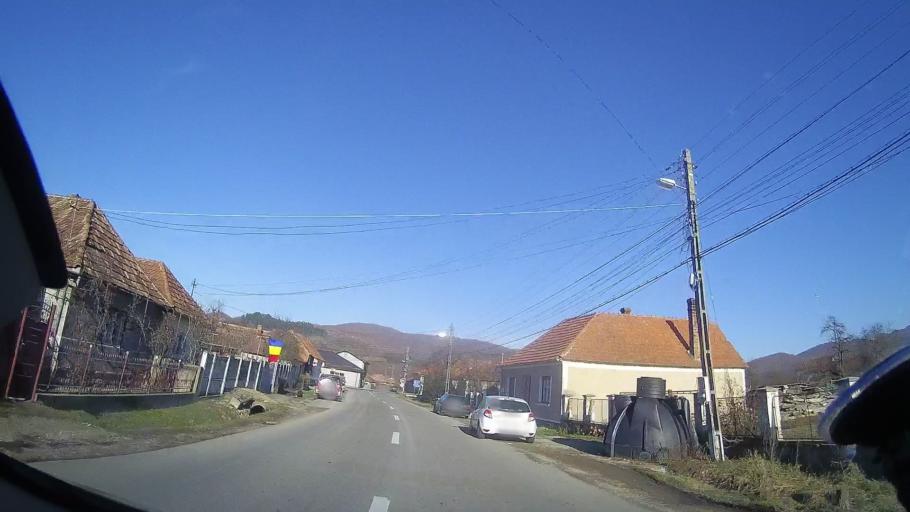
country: RO
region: Bihor
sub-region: Comuna Borod
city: Borod
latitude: 46.9901
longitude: 22.6175
